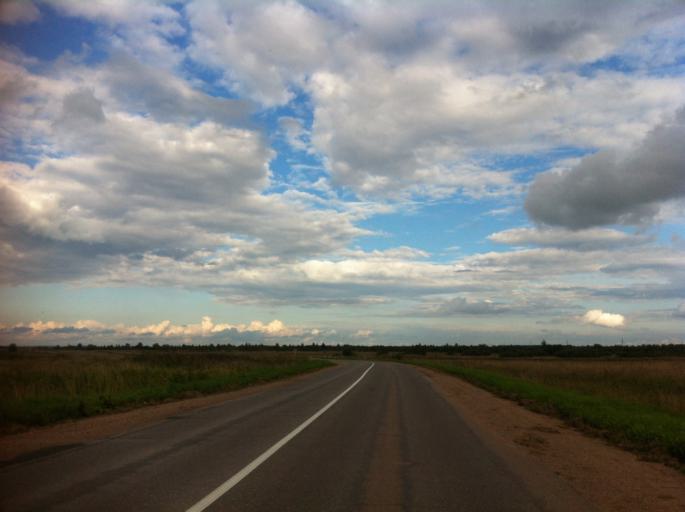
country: RU
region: Pskov
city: Izborsk
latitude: 57.8362
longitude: 28.0499
